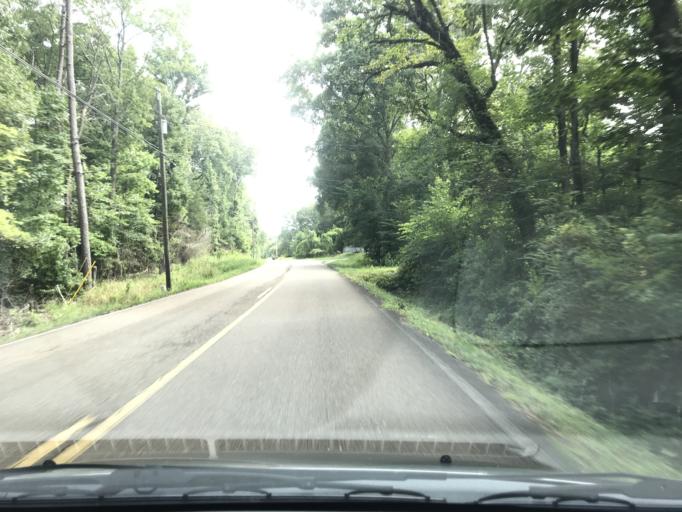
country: US
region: Tennessee
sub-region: Hamilton County
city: Lakesite
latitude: 35.2008
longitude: -85.1009
